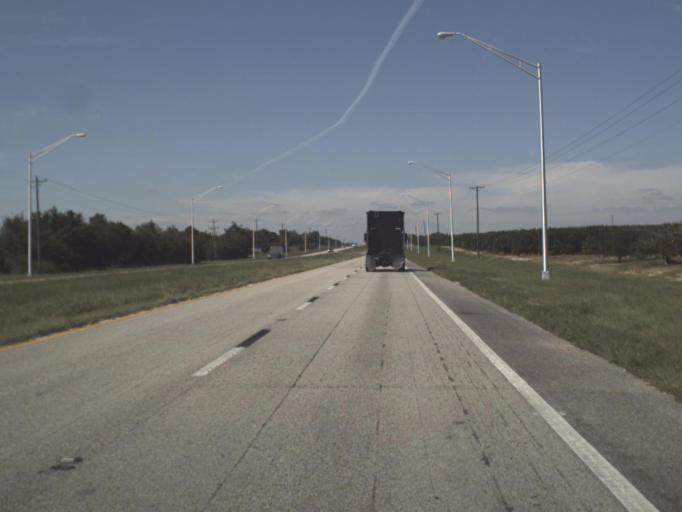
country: US
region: Florida
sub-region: Highlands County
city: Lake Placid
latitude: 27.3762
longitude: -81.4035
